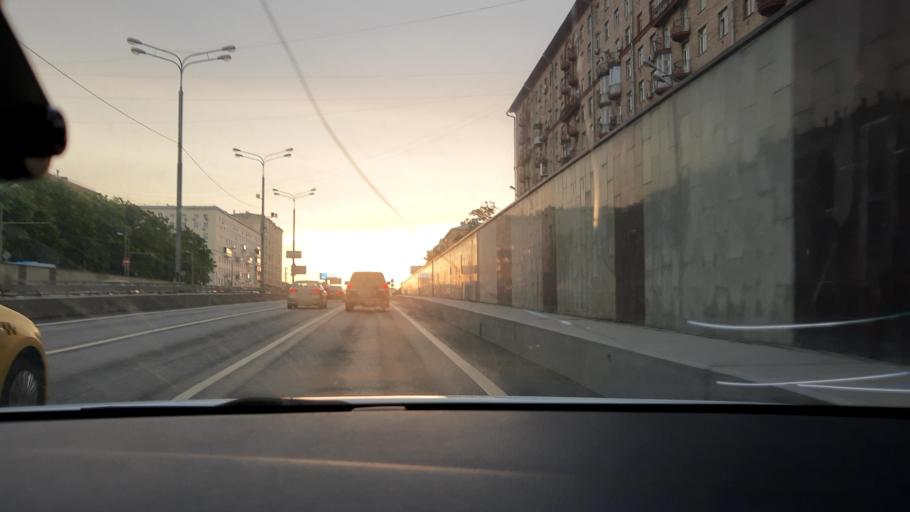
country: RU
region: Moskovskaya
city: Koptevo
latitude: 55.8090
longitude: 37.4985
